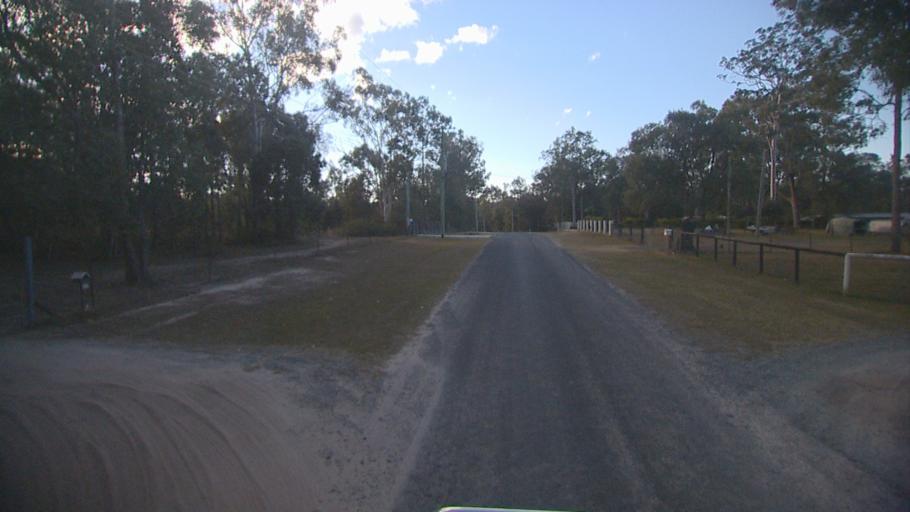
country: AU
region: Queensland
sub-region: Logan
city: Cedar Vale
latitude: -27.8453
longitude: 153.1107
